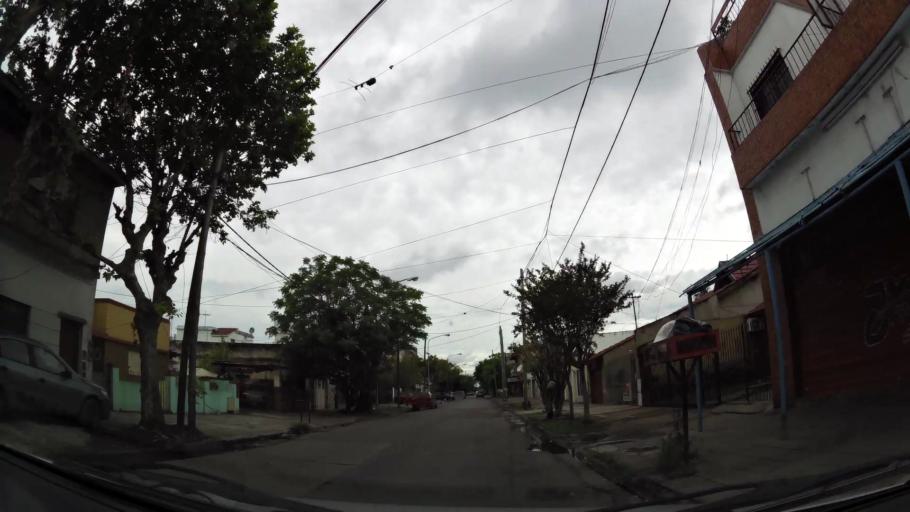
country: AR
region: Buenos Aires
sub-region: Partido de Lanus
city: Lanus
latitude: -34.7269
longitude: -58.3696
